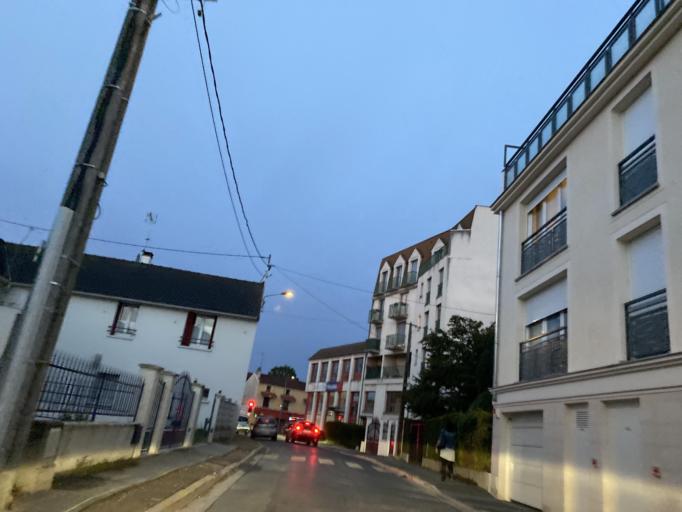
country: FR
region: Ile-de-France
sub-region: Departement des Yvelines
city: Houilles
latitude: 48.9262
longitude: 2.1951
